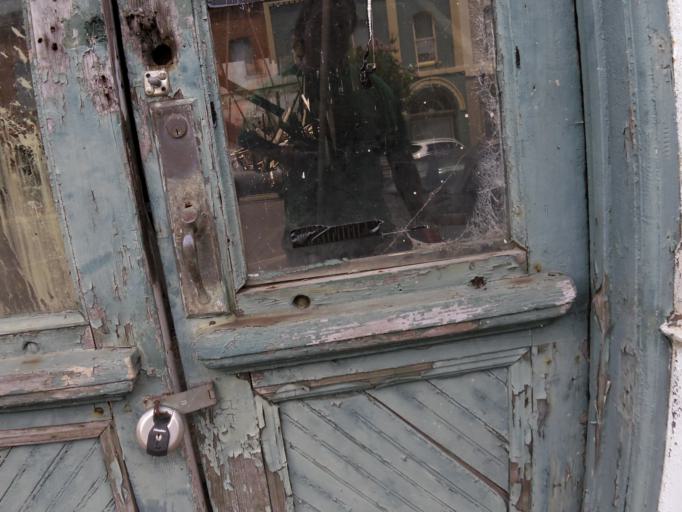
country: US
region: Mississippi
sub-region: Lauderdale County
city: Meridian
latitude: 32.3616
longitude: -88.7010
